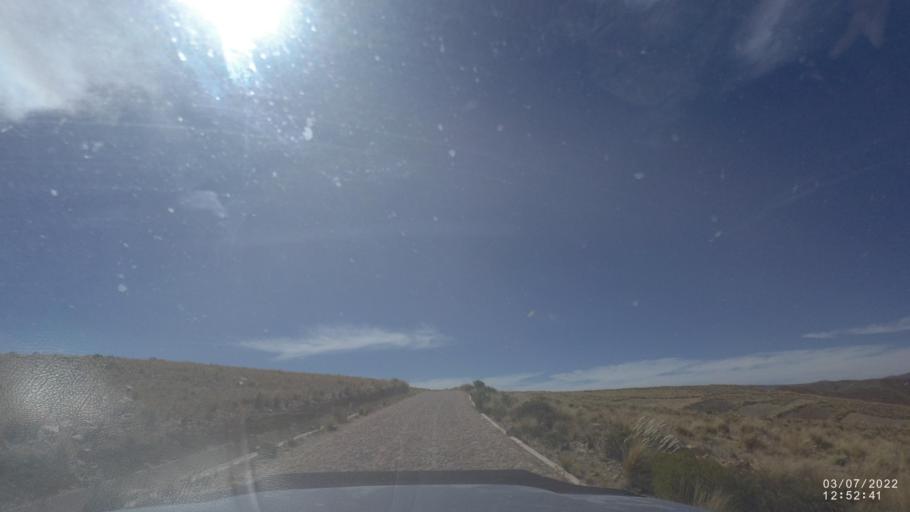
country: BO
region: Cochabamba
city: Irpa Irpa
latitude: -17.7488
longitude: -66.6610
